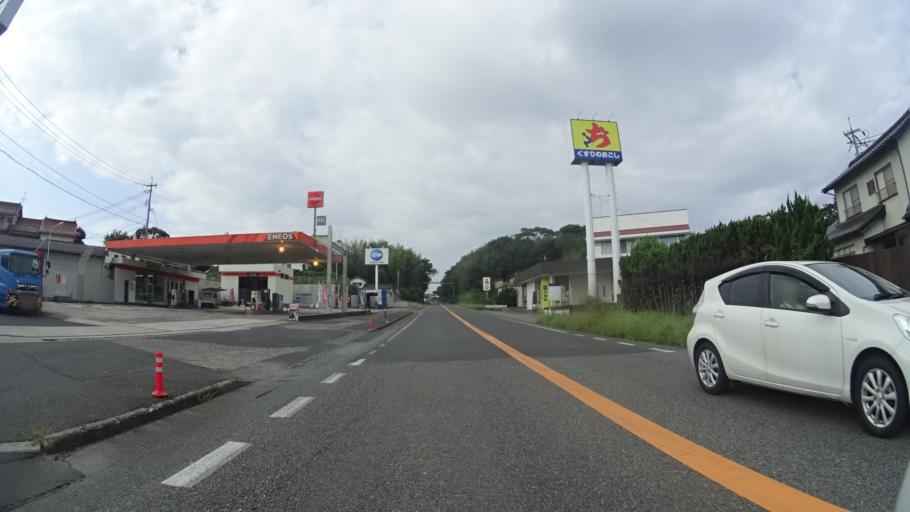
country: JP
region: Shimane
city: Odacho-oda
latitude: 35.2210
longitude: 132.5121
